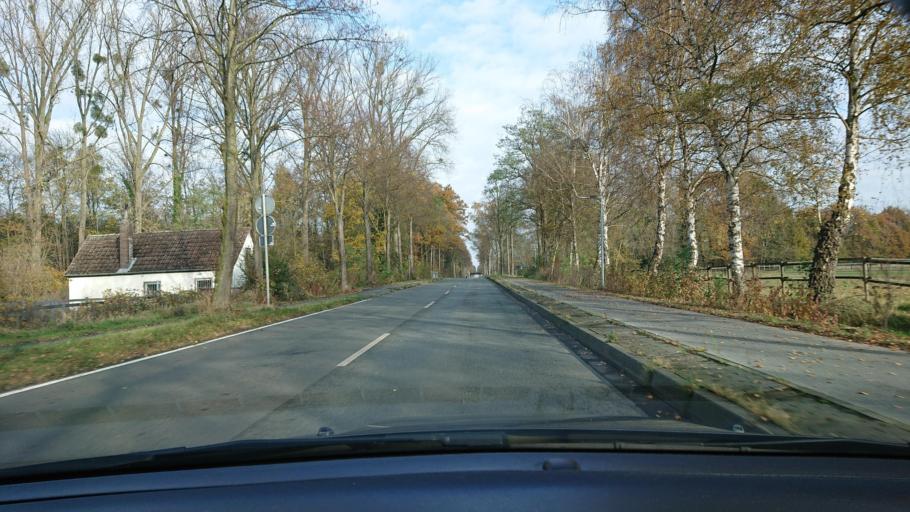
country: DE
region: North Rhine-Westphalia
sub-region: Regierungsbezirk Arnsberg
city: Lippstadt
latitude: 51.6977
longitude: 8.3576
